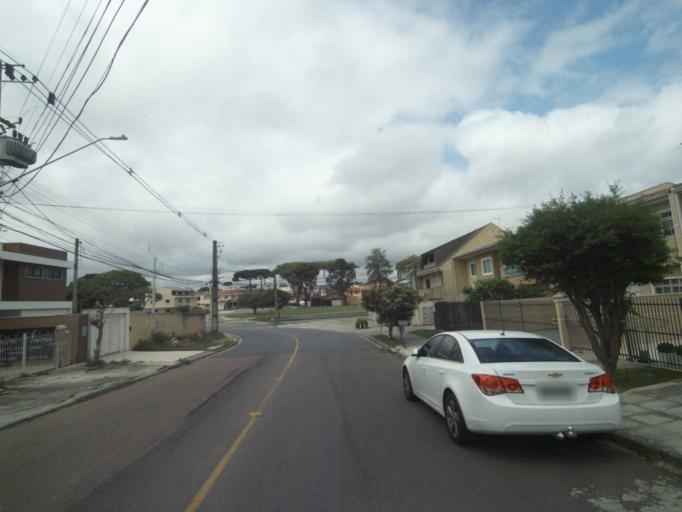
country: BR
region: Parana
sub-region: Pinhais
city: Pinhais
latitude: -25.4339
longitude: -49.2220
